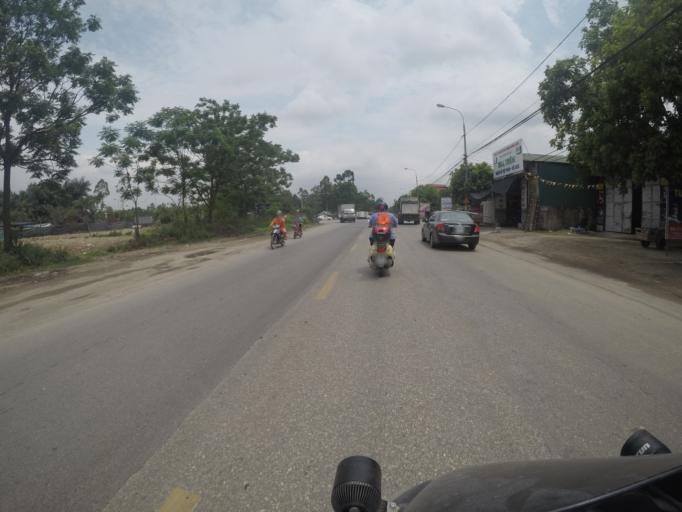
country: VN
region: Ha Noi
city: Soc Son
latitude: 21.2294
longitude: 105.8490
